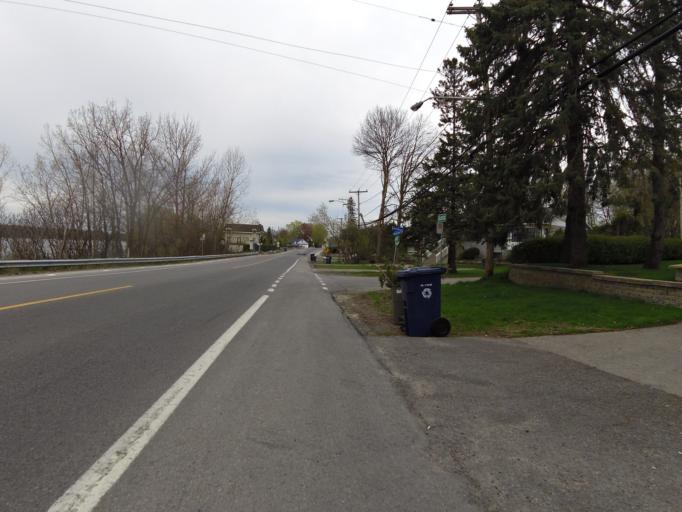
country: CA
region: Quebec
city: Dollard-Des Ormeaux
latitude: 45.5207
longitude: -73.8295
